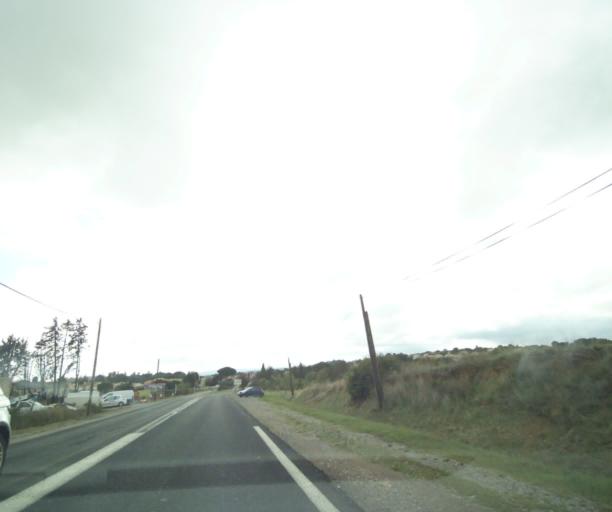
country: FR
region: Languedoc-Roussillon
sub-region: Departement de l'Herault
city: Pignan
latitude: 43.5897
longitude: 3.7703
